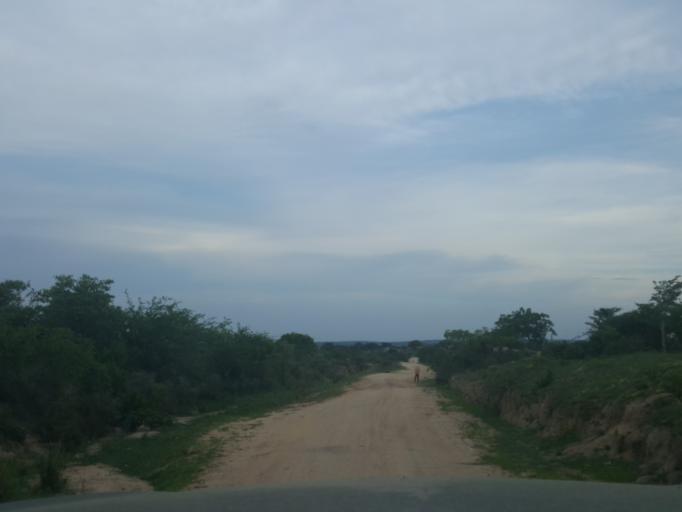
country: ZA
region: Limpopo
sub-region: Mopani District Municipality
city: Hoedspruit
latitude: -24.5842
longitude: 30.9827
